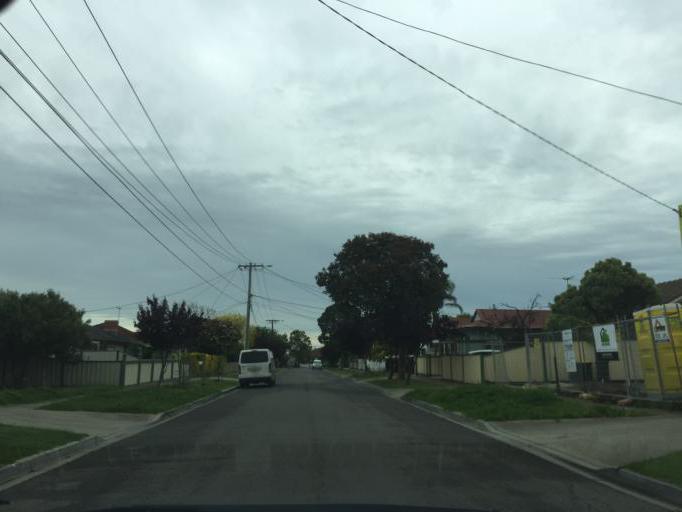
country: AU
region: Victoria
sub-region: Maribyrnong
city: Braybrook
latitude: -37.7819
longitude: 144.8459
